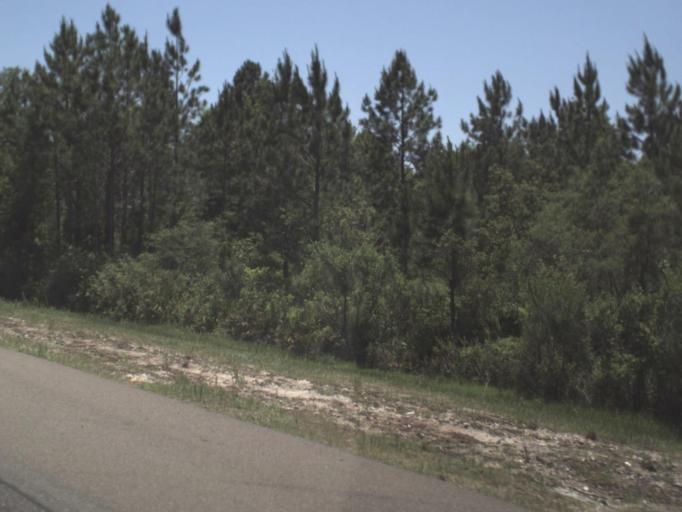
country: US
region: Florida
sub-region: Duval County
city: Baldwin
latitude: 30.2648
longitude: -81.8677
